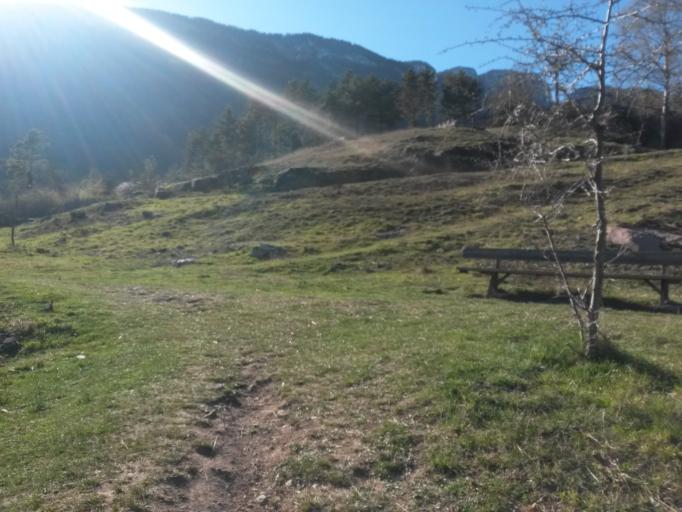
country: IT
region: Trentino-Alto Adige
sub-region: Bolzano
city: San Paolo
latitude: 46.4697
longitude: 11.2453
